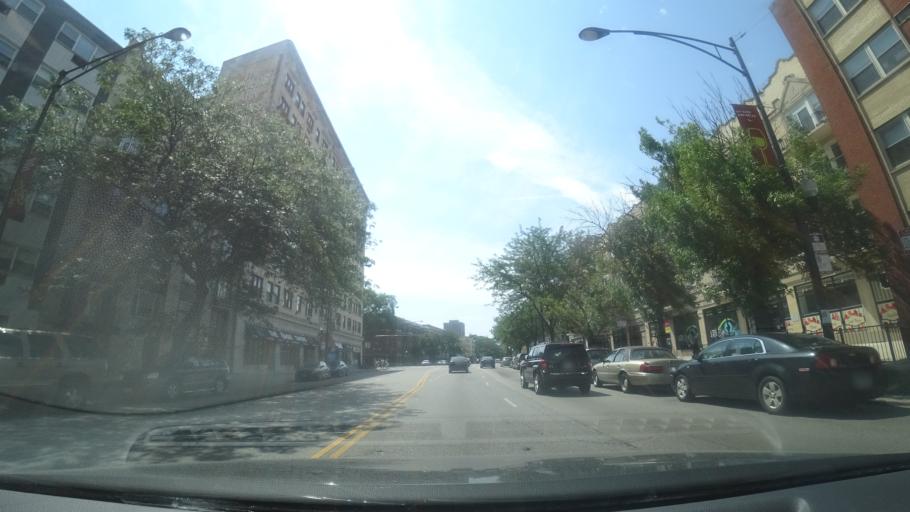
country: US
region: Illinois
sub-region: Cook County
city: Evanston
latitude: 42.0064
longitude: -87.6612
